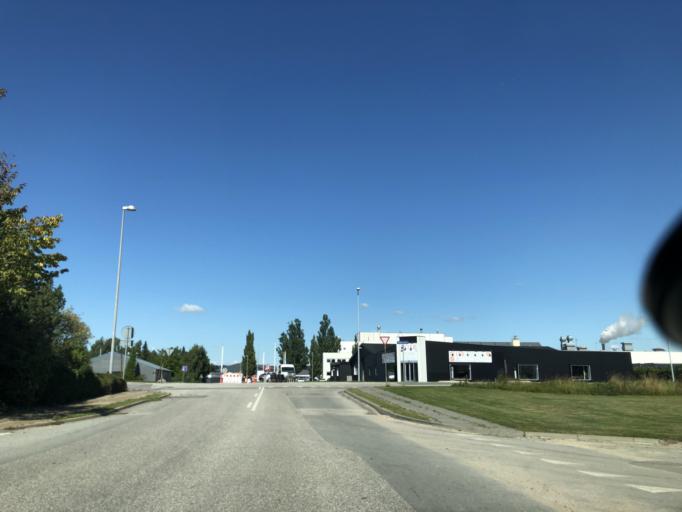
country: DK
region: North Denmark
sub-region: Mariagerfjord Kommune
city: Hobro
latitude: 56.6492
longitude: 9.8026
